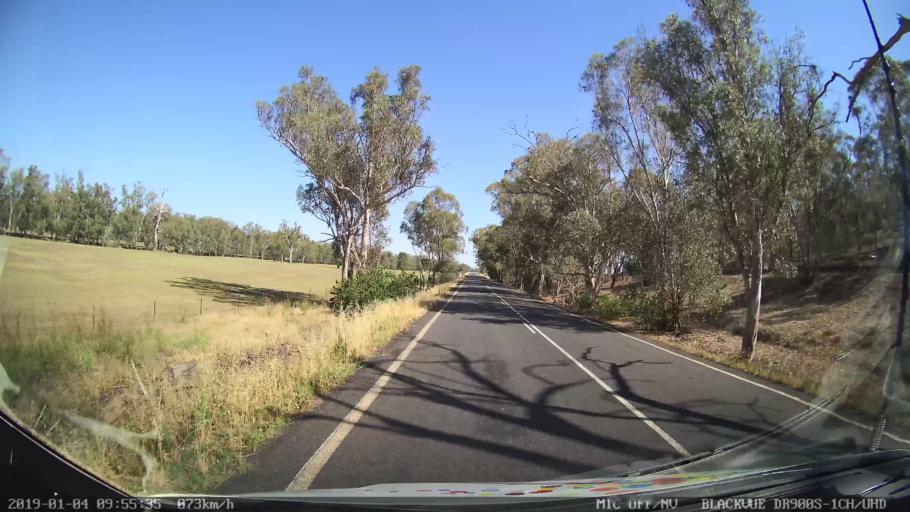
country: AU
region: New South Wales
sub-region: Cabonne
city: Canowindra
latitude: -33.5333
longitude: 148.4031
